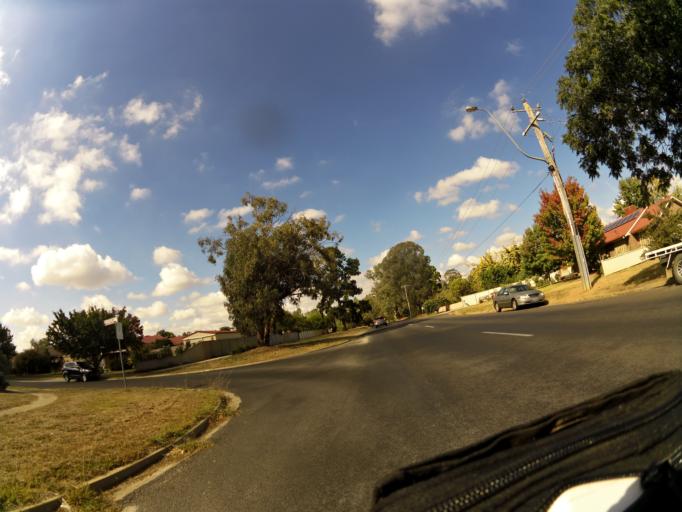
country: AU
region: Victoria
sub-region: Benalla
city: Benalla
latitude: -36.5593
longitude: 145.9949
